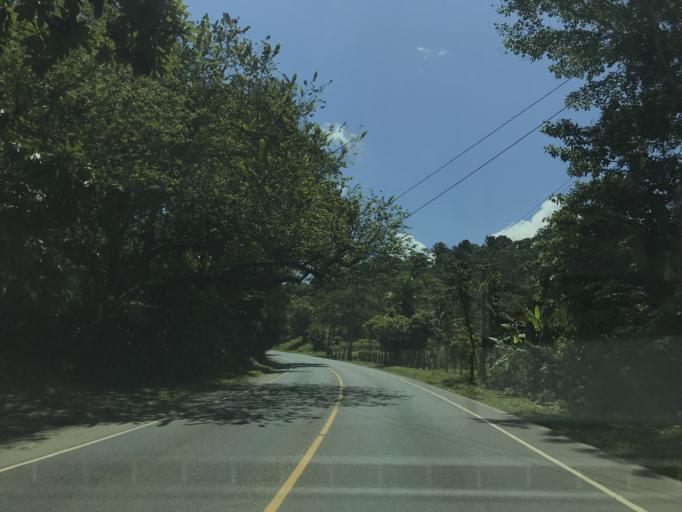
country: GT
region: Izabal
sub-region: Municipio de Puerto Barrios
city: Puerto Barrios
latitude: 15.6641
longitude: -88.5576
